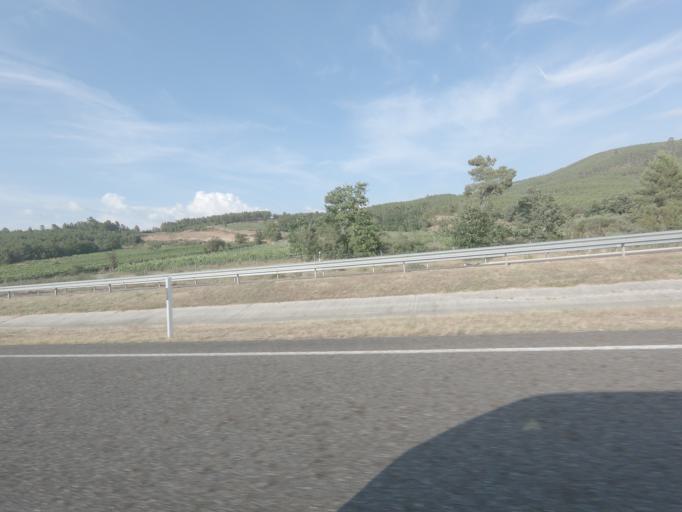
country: ES
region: Galicia
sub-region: Provincia de Ourense
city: Oimbra
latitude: 41.8689
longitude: -7.4328
